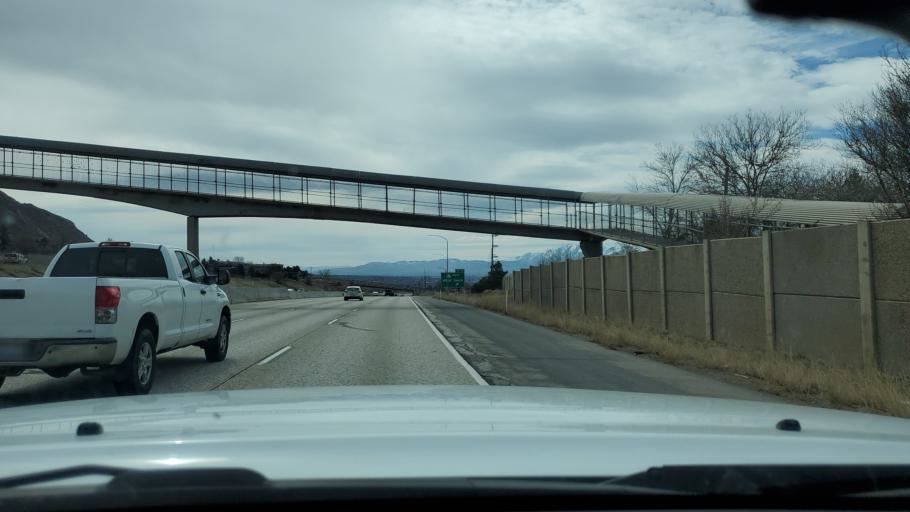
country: US
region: Utah
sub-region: Salt Lake County
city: Mount Olympus
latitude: 40.6785
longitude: -111.7990
